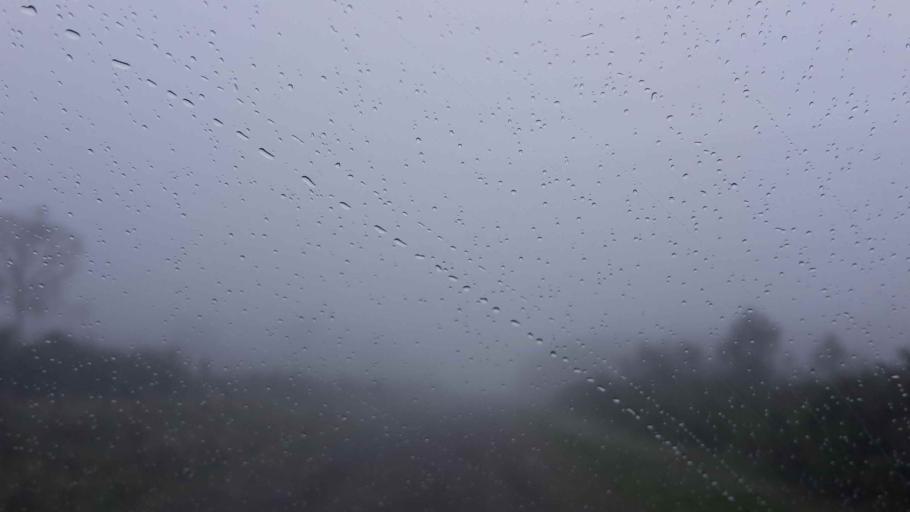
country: BO
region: Cochabamba
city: Colomi
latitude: -17.1094
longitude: -65.9726
